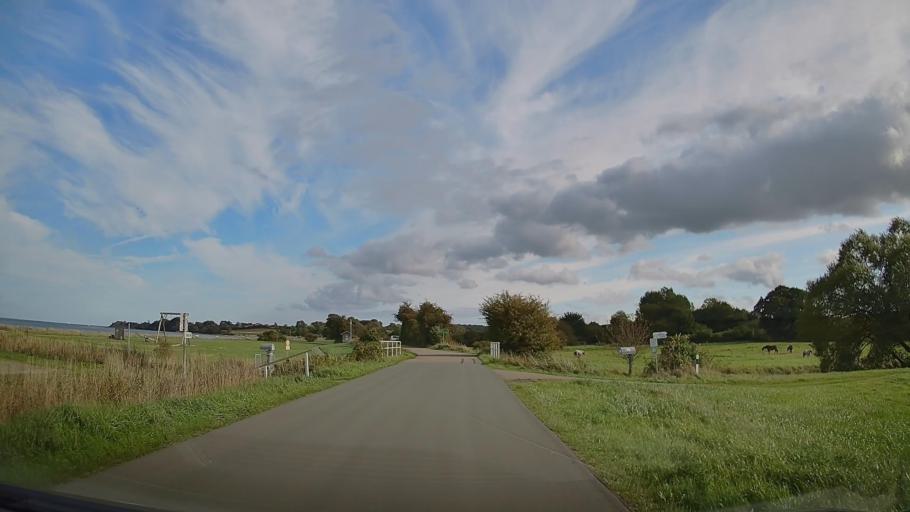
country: DE
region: Schleswig-Holstein
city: Steinberg
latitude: 54.7966
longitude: 9.7674
